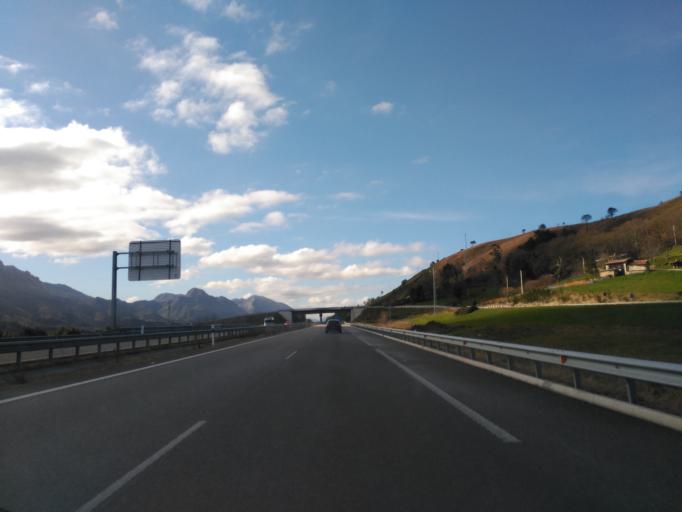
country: ES
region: Asturias
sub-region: Province of Asturias
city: Llanes
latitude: 43.4031
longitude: -4.7333
